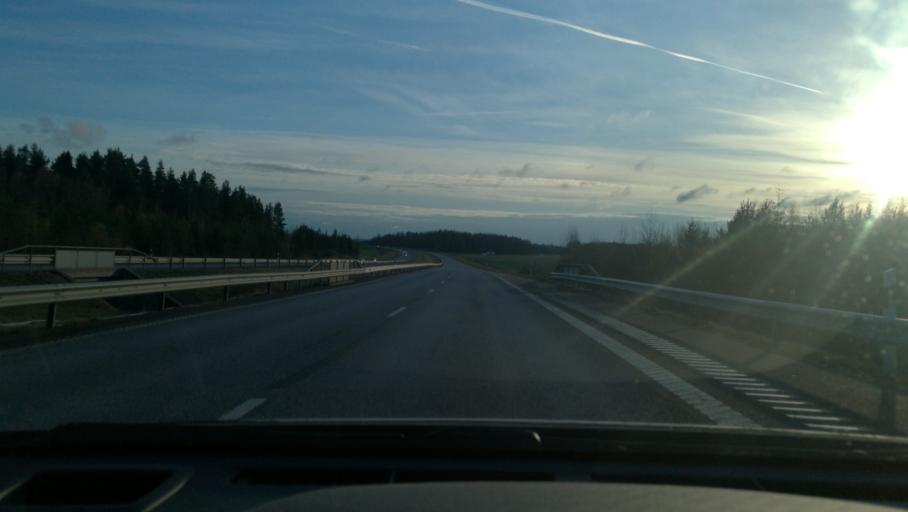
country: SE
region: Vaestmanland
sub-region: Arboga Kommun
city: Arboga
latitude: 59.4616
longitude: 15.8979
